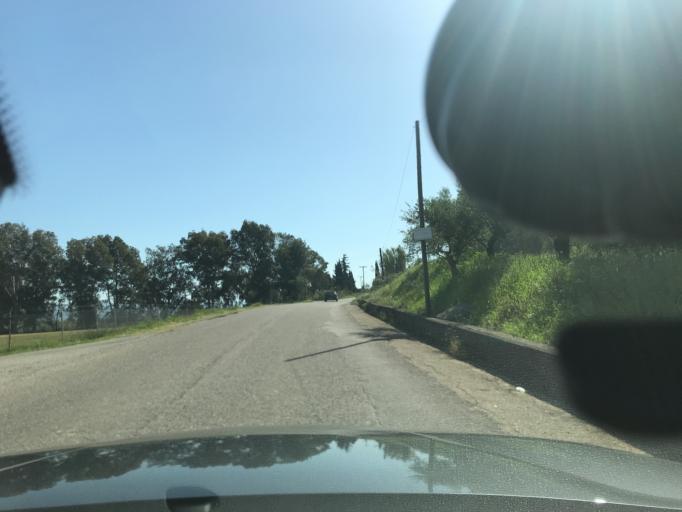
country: GR
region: West Greece
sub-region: Nomos Ileias
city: Epitalion
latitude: 37.6415
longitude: 21.5109
